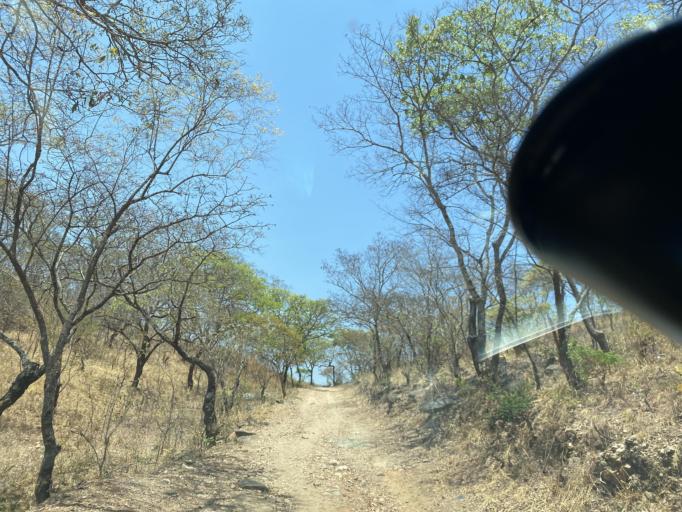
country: ZM
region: Lusaka
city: Kafue
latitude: -15.8056
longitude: 28.4282
